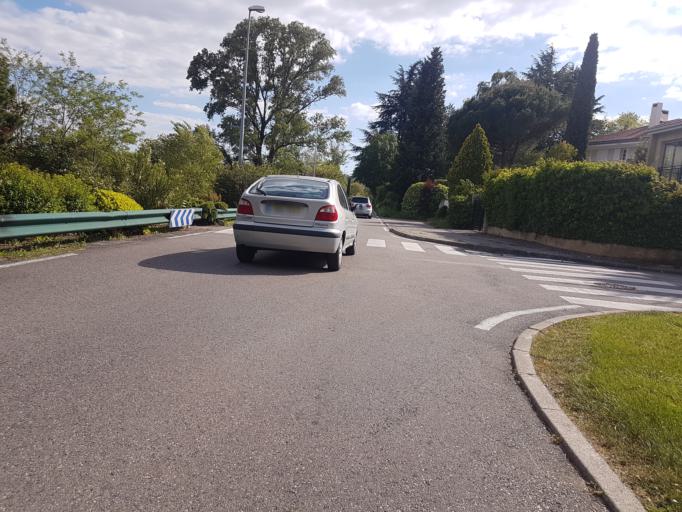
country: FR
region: Rhone-Alpes
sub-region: Departement de l'Ardeche
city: Guilherand-Granges
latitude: 44.9257
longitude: 4.8746
